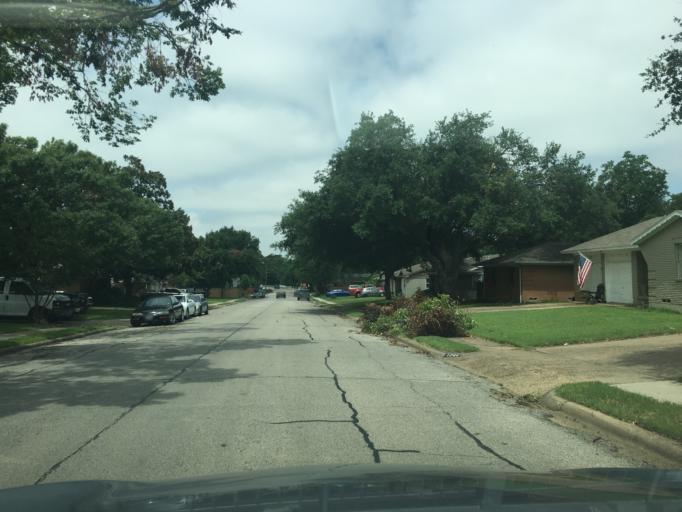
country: US
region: Texas
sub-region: Dallas County
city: Richardson
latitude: 32.9468
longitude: -96.7619
